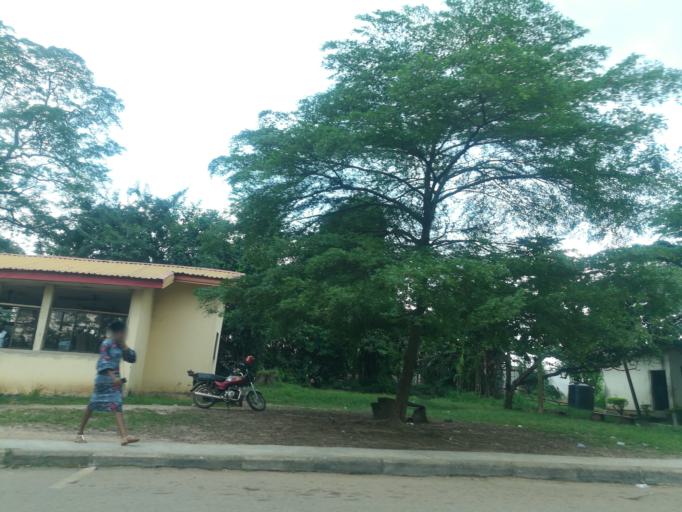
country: NG
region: Oyo
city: Ibadan
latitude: 7.4420
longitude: 3.9059
